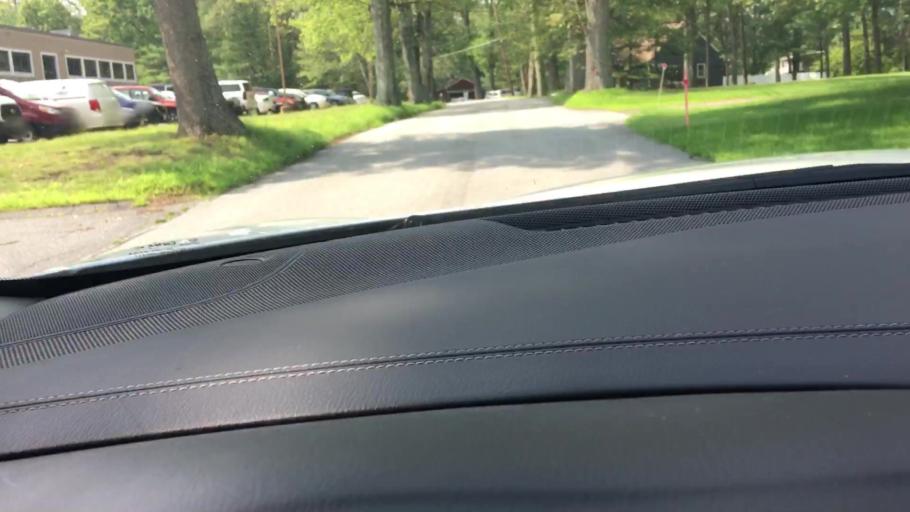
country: US
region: Massachusetts
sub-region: Worcester County
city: Northborough
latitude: 42.2910
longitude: -71.6575
